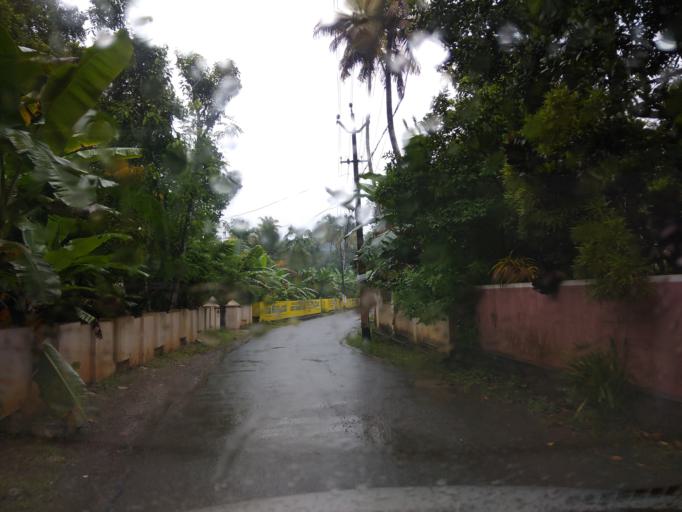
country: IN
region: Kerala
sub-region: Ernakulam
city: Perumpavur
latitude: 10.1131
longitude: 76.4995
